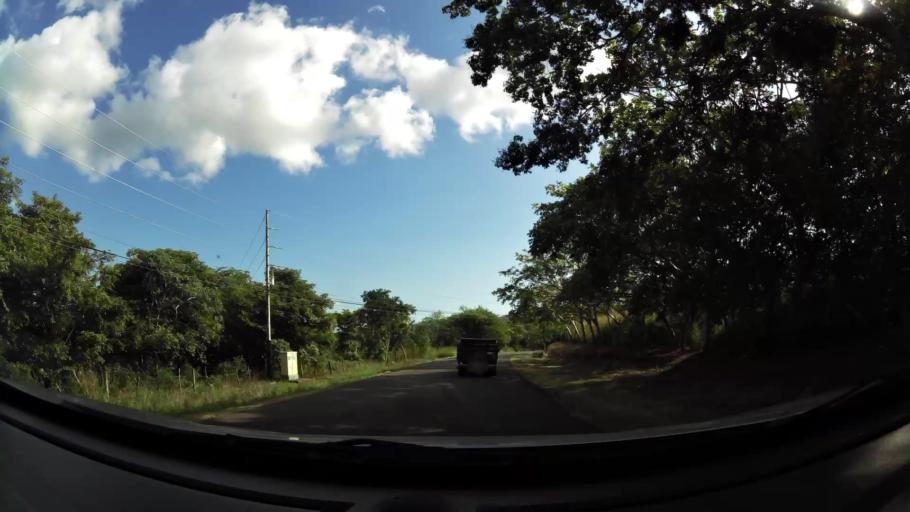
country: CR
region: Guanacaste
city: Sardinal
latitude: 10.5474
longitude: -85.6774
